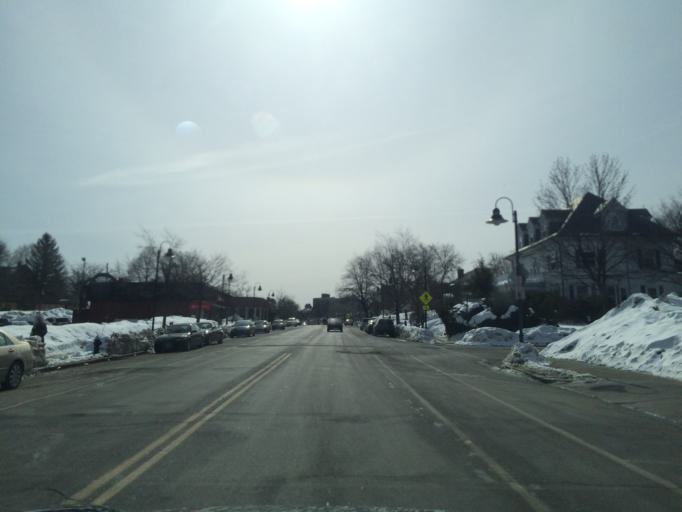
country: US
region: Massachusetts
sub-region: Norfolk County
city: Brookline
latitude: 42.3483
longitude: -71.1294
